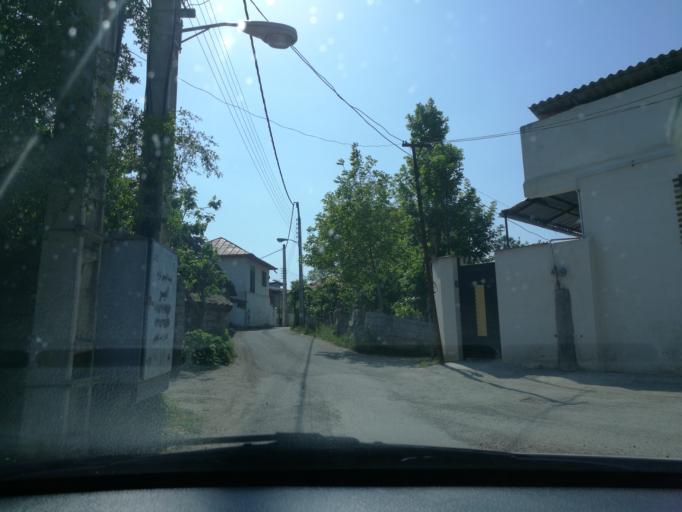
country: IR
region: Mazandaran
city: Chalus
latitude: 36.6678
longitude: 51.4329
